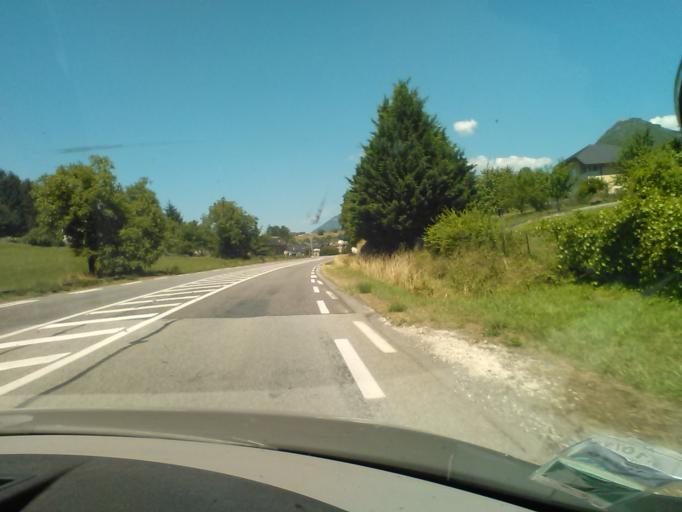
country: FR
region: Rhone-Alpes
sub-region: Departement de la Savoie
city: Les Marches
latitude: 45.5254
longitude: 5.9936
